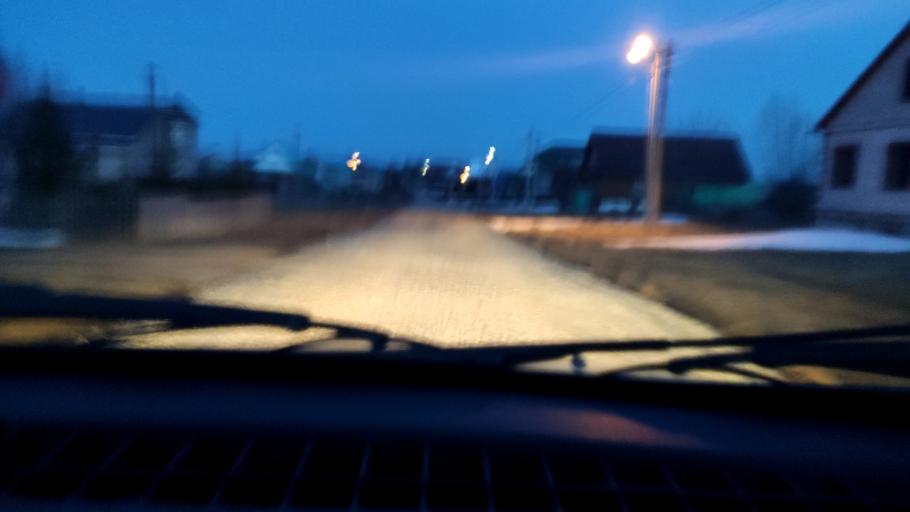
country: RU
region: Bashkortostan
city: Iglino
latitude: 54.7930
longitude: 56.3119
